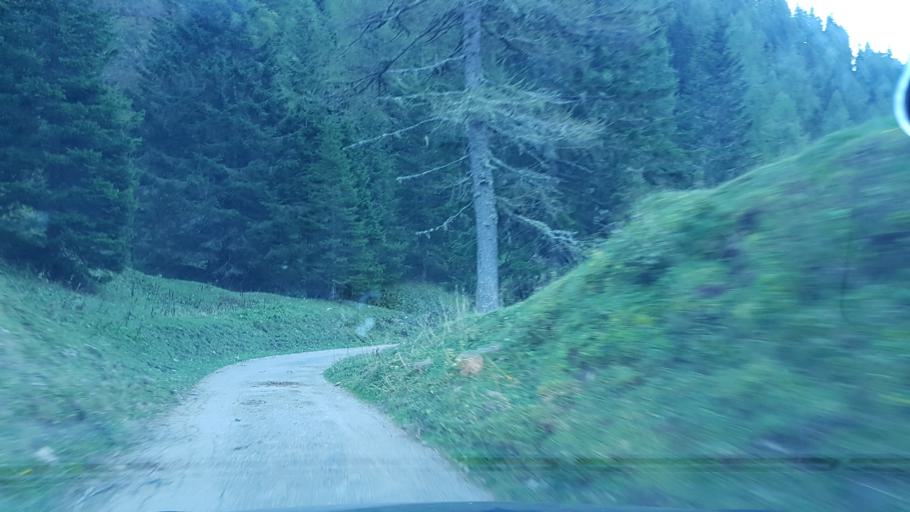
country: IT
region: Veneto
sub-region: Provincia di Belluno
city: Fusine
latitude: 46.3608
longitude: 12.0912
